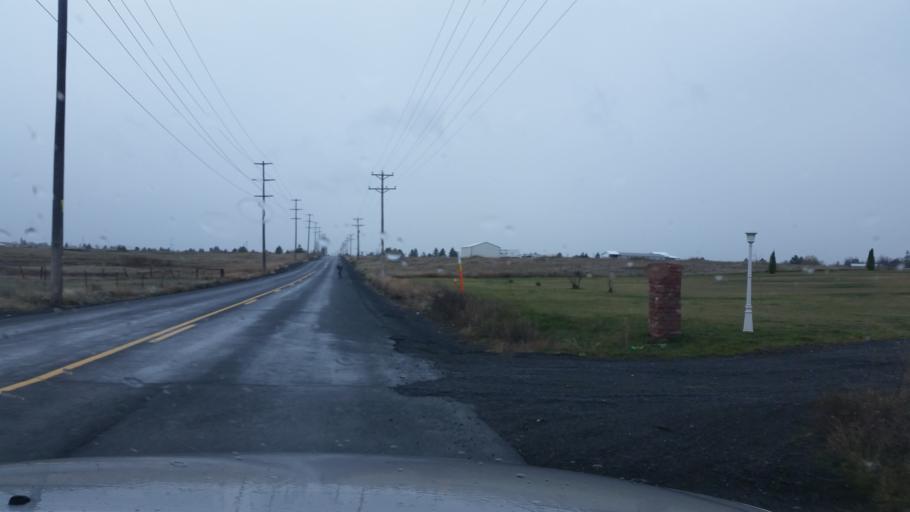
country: US
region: Washington
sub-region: Spokane County
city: Airway Heights
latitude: 47.6582
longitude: -117.6039
